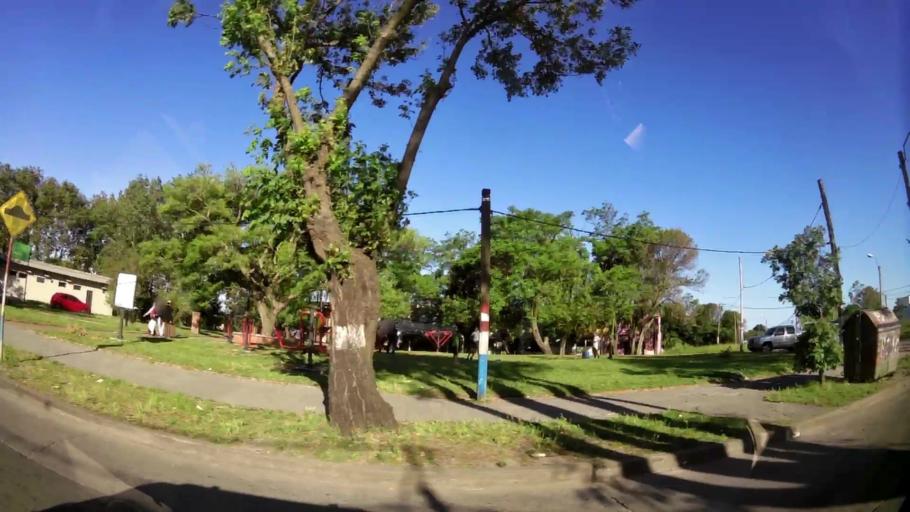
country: UY
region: Canelones
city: La Paz
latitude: -34.8282
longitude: -56.2006
